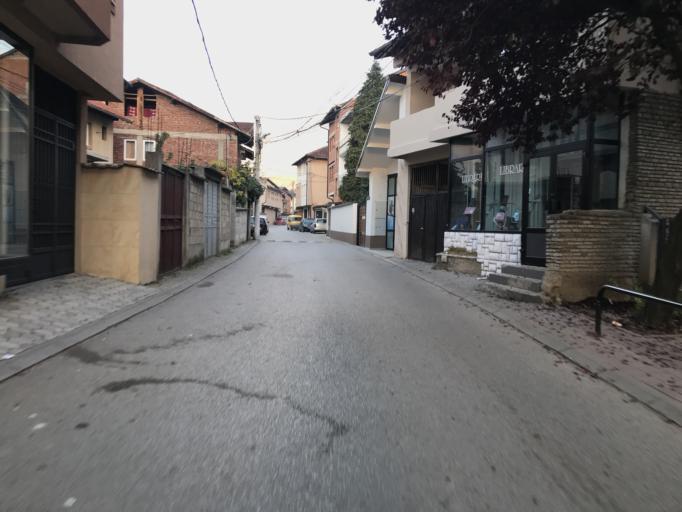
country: XK
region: Pec
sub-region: Komuna e Pejes
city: Peje
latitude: 42.6588
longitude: 20.3003
